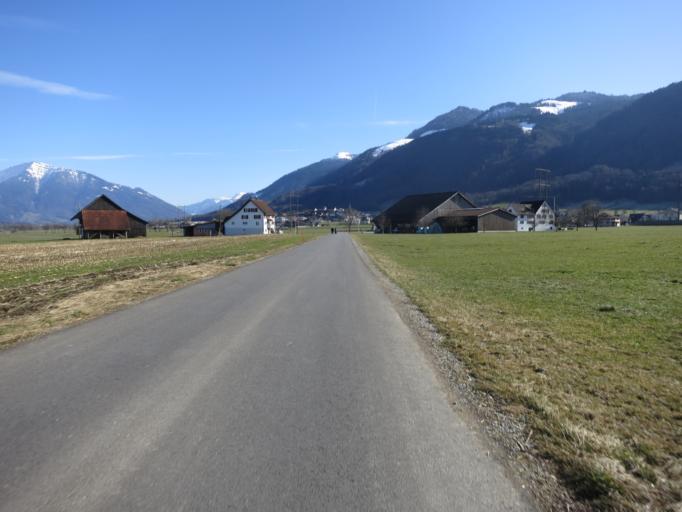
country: CH
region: Schwyz
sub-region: Bezirk March
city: Schubelbach
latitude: 47.1808
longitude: 8.9258
